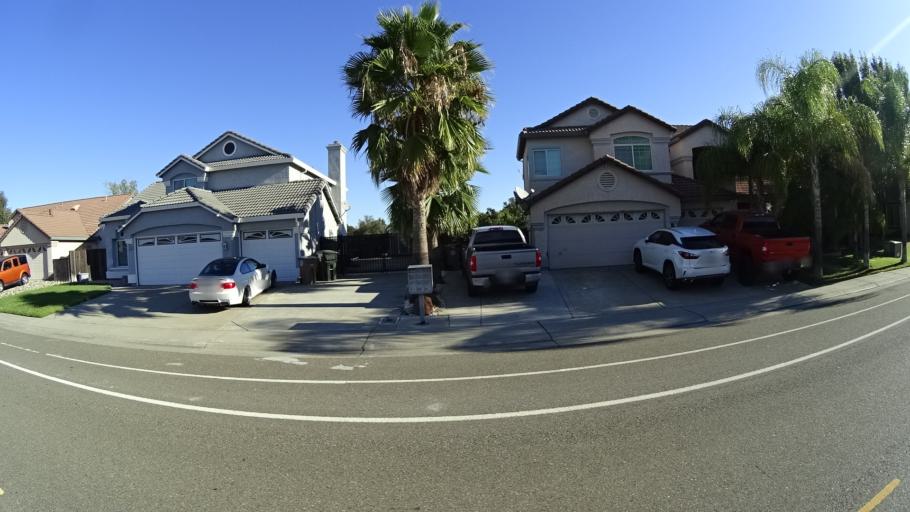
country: US
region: California
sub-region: Sacramento County
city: Elk Grove
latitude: 38.4438
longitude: -121.3807
